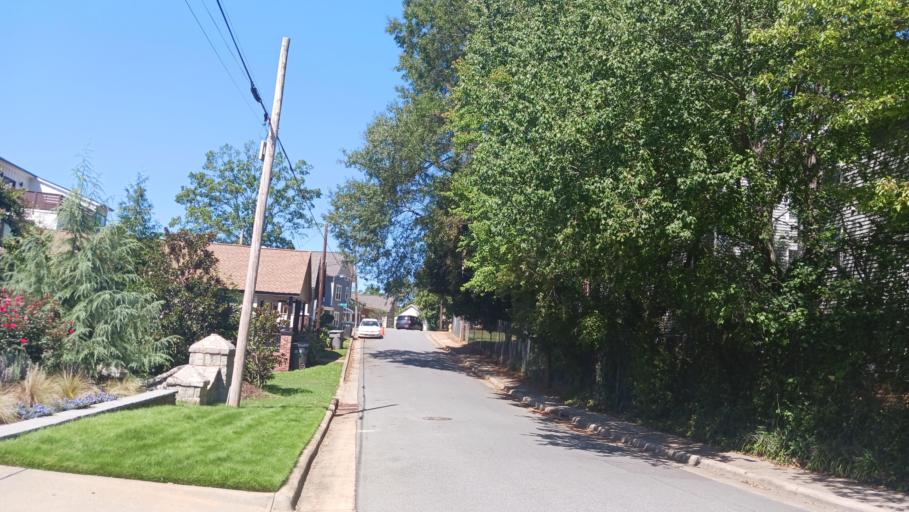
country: US
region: North Carolina
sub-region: Mecklenburg County
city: Charlotte
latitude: 35.2077
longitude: -80.8287
